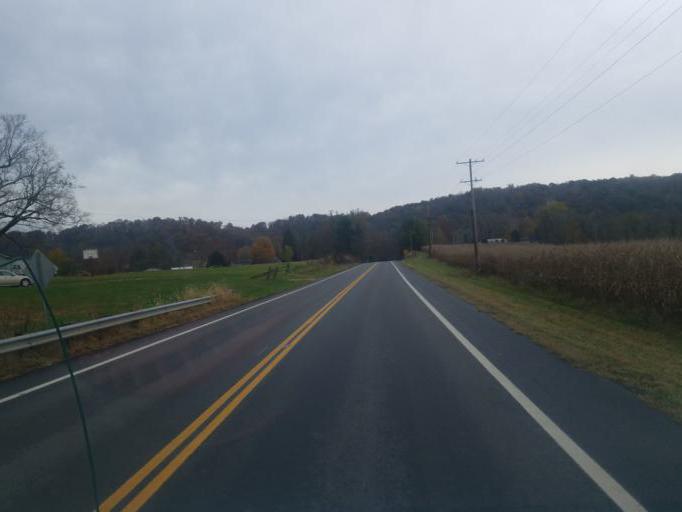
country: US
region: Ohio
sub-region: Washington County
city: Beverly
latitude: 39.5634
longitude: -81.5846
